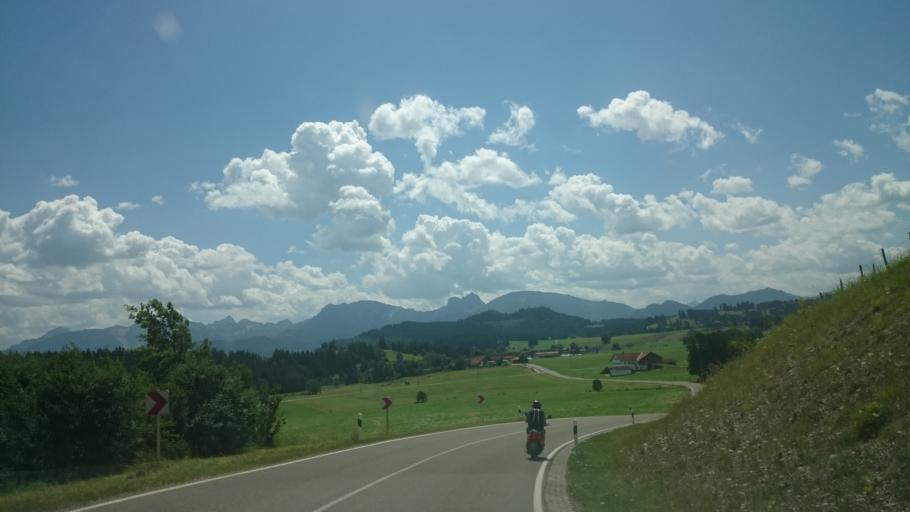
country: DE
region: Bavaria
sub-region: Swabia
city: Seeg
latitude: 47.6453
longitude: 10.6056
